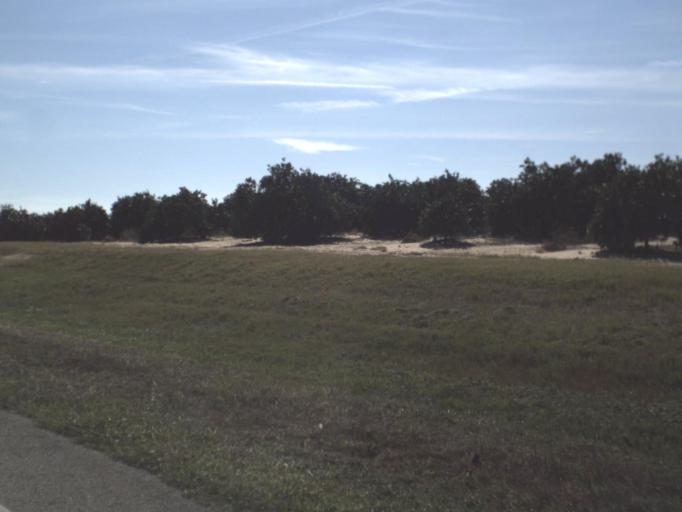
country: US
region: Florida
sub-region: Highlands County
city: Lake Placid
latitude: 27.2205
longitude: -81.3288
